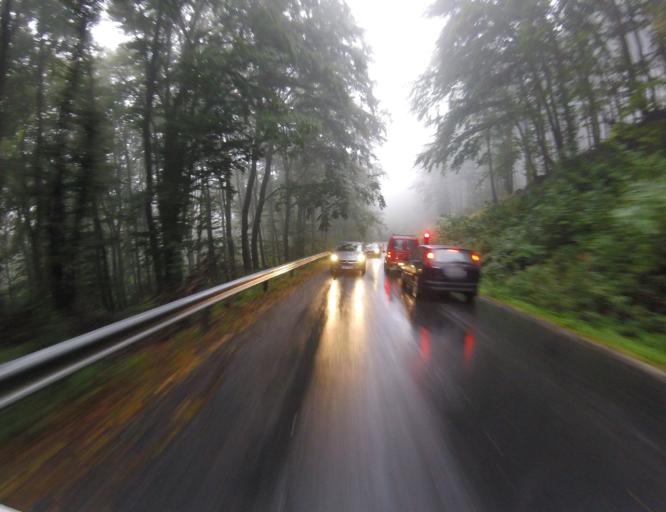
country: HU
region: Pest
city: Pilisszentkereszt
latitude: 47.7183
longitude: 18.8659
